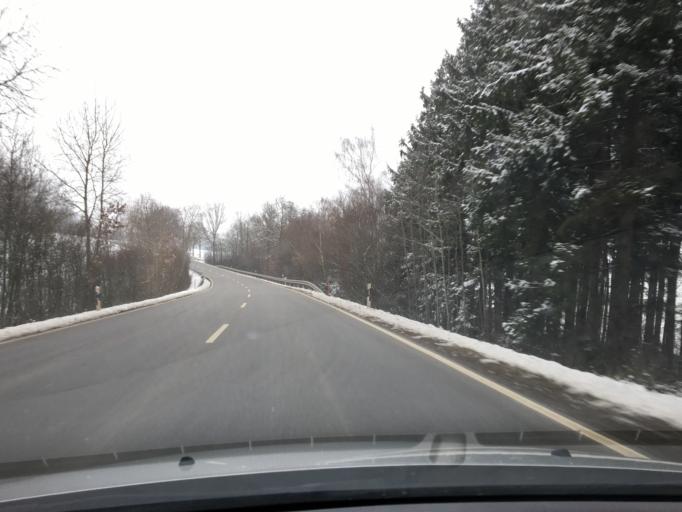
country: DE
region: Bavaria
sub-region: Lower Bavaria
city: Vilsbiburg
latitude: 48.4370
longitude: 12.3787
